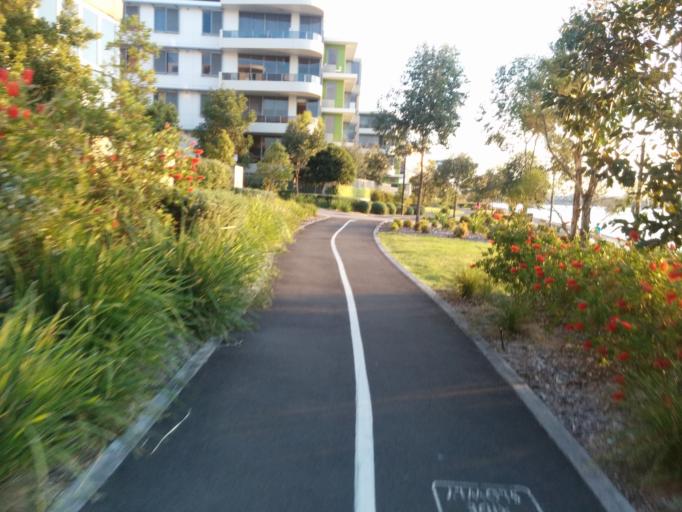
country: AU
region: New South Wales
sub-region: Canada Bay
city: Rhodes
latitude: -33.8241
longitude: 151.0865
